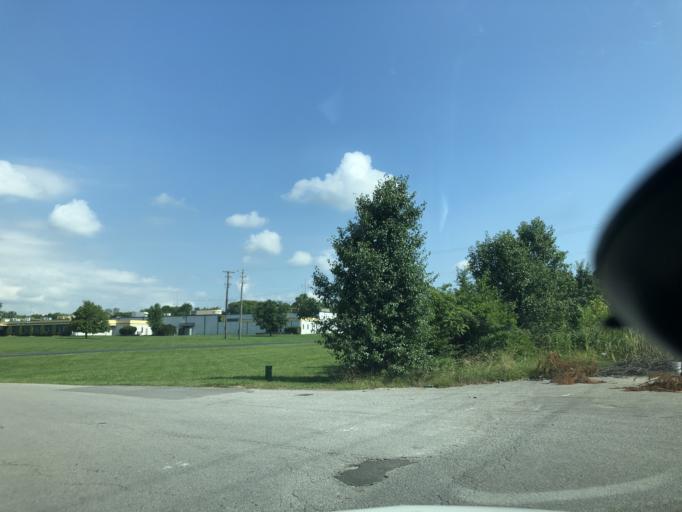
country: US
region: Tennessee
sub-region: Rutherford County
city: La Vergne
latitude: 36.0238
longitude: -86.6061
